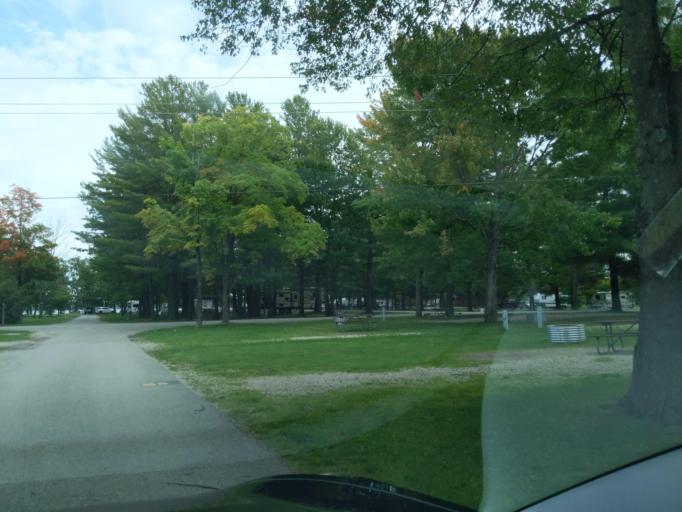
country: US
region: Michigan
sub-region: Wexford County
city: Cadillac
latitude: 44.2382
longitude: -85.4527
